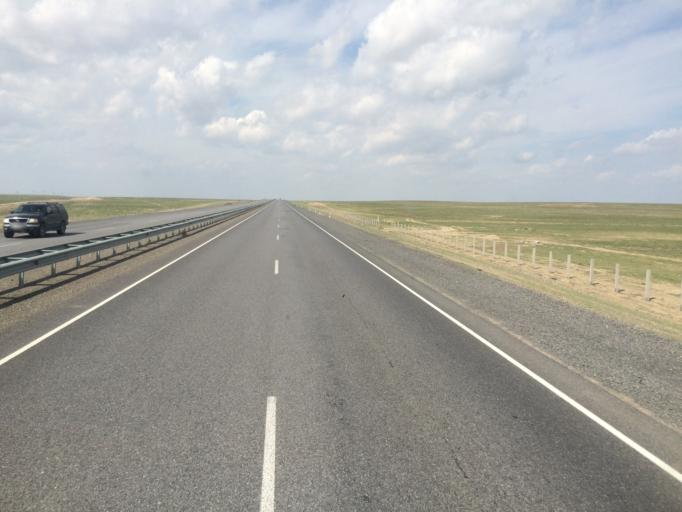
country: KZ
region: Qyzylorda
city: Shalqiya
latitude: 43.8582
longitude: 67.4016
